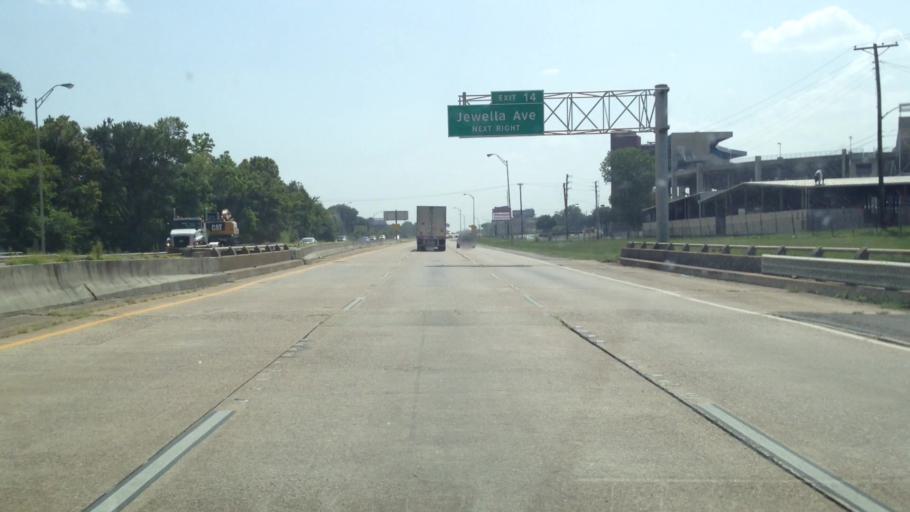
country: US
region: Louisiana
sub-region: Caddo Parish
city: Shreveport
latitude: 32.4749
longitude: -93.7883
